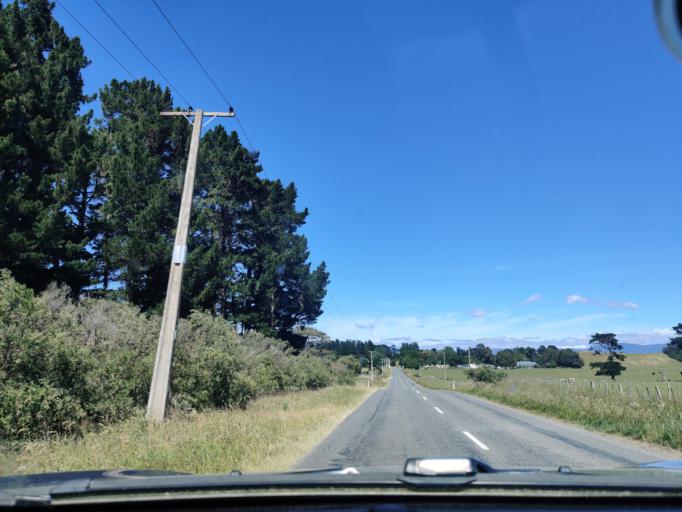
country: NZ
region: Wellington
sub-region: South Wairarapa District
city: Waipawa
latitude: -41.2260
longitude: 175.3476
